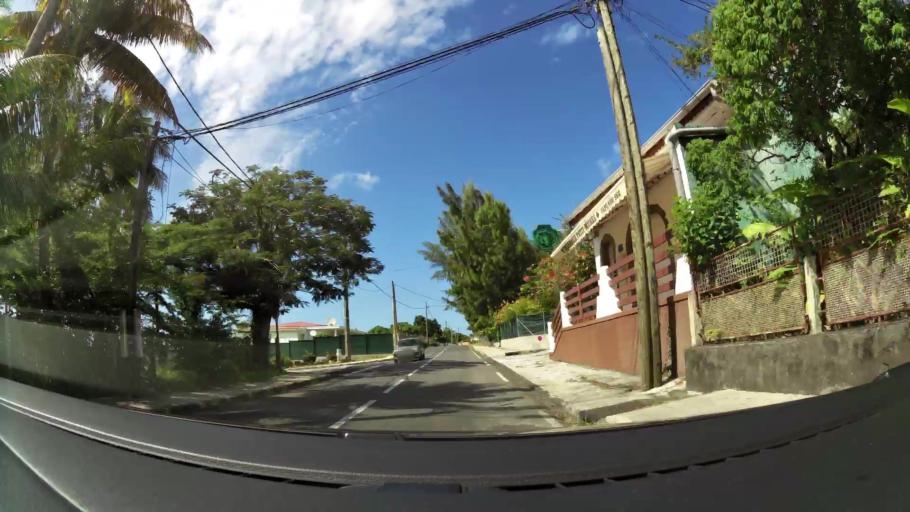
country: GP
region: Guadeloupe
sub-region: Guadeloupe
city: Saint-Claude
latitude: 16.0161
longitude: -61.7131
